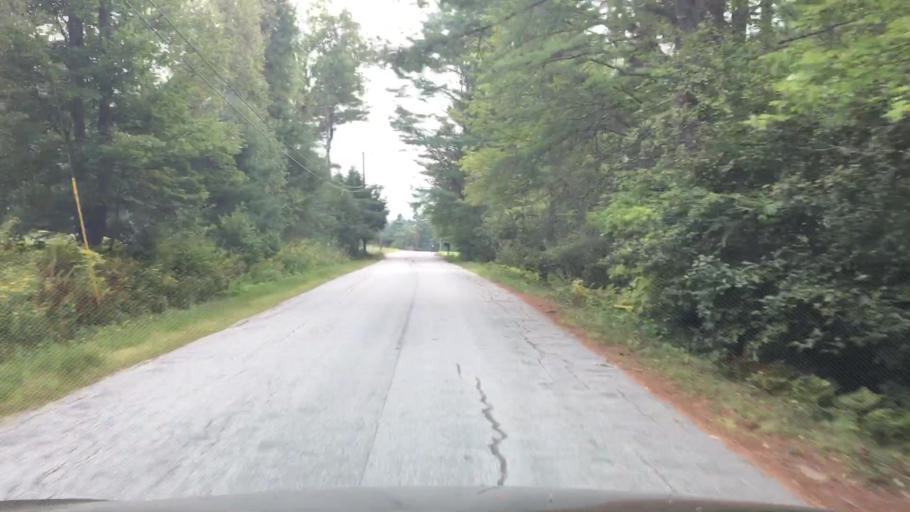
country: US
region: New Hampshire
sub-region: Grafton County
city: Littleton
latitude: 44.3177
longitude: -71.8795
